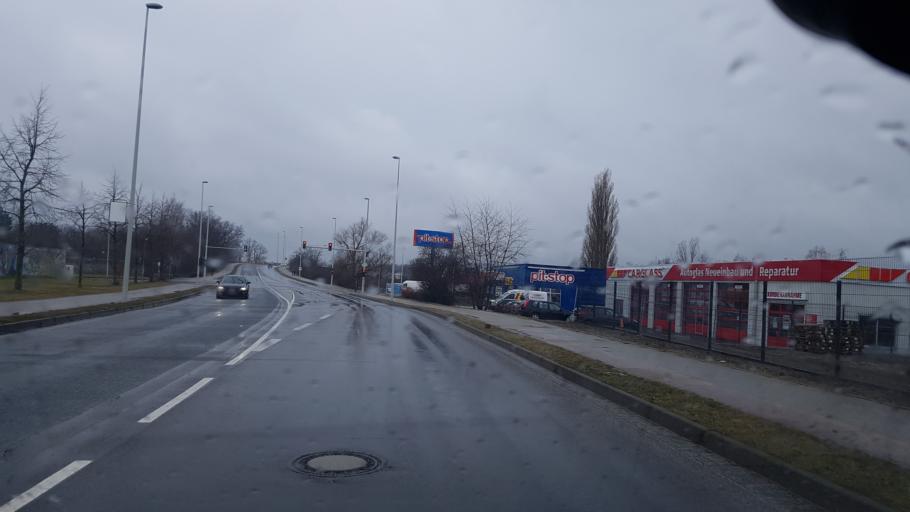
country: DE
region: Brandenburg
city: Cottbus
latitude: 51.7230
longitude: 14.3190
